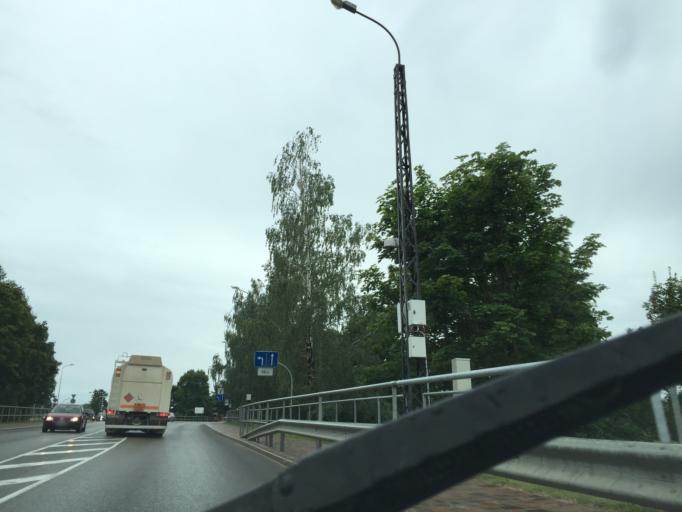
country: LV
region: Jekabpils Rajons
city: Jekabpils
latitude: 56.4985
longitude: 25.8784
